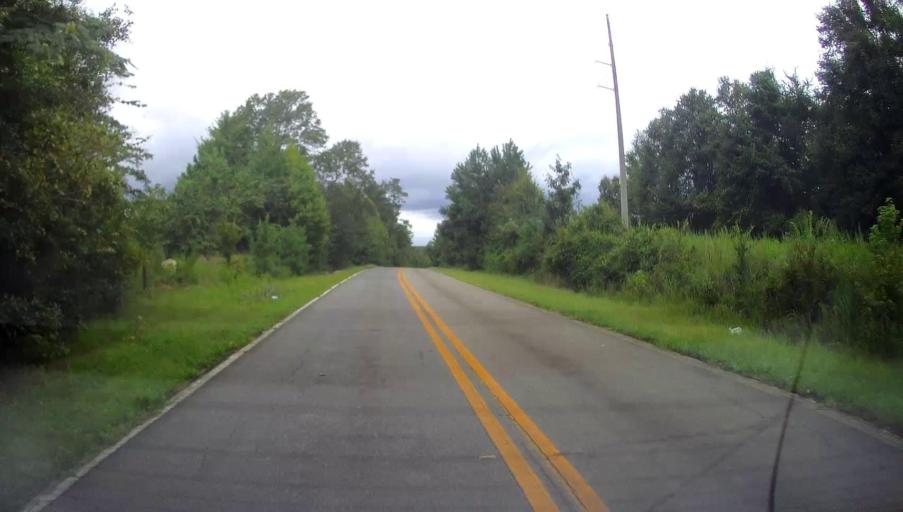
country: US
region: Georgia
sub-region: Bibb County
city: Macon
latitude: 32.7956
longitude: -83.5257
